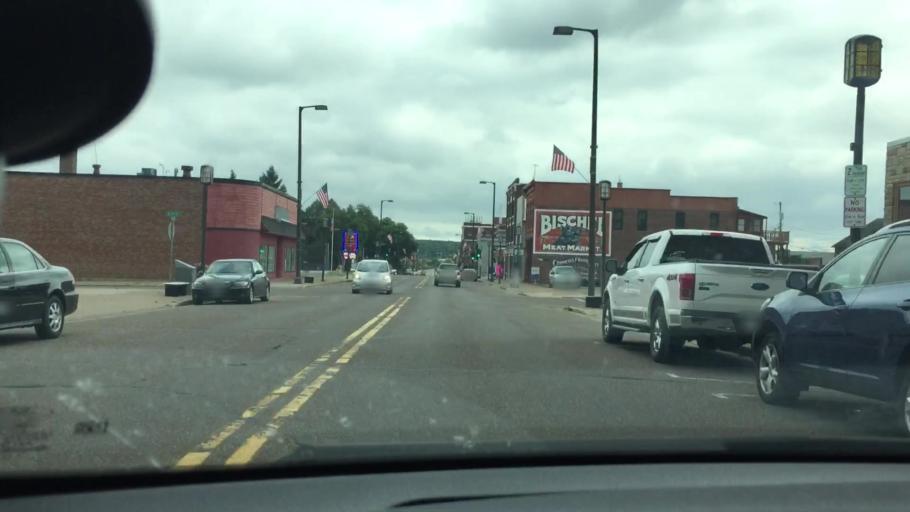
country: US
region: Wisconsin
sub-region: Chippewa County
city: Chippewa Falls
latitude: 44.9391
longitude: -91.3960
